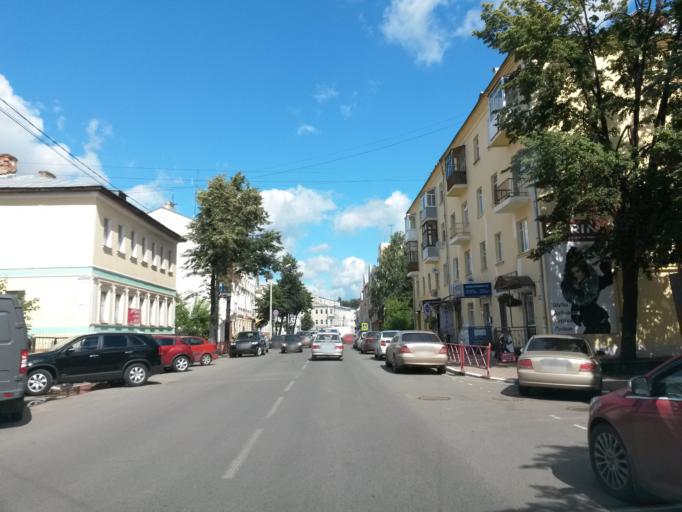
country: RU
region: Jaroslavl
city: Yaroslavl
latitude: 57.6233
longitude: 39.8817
